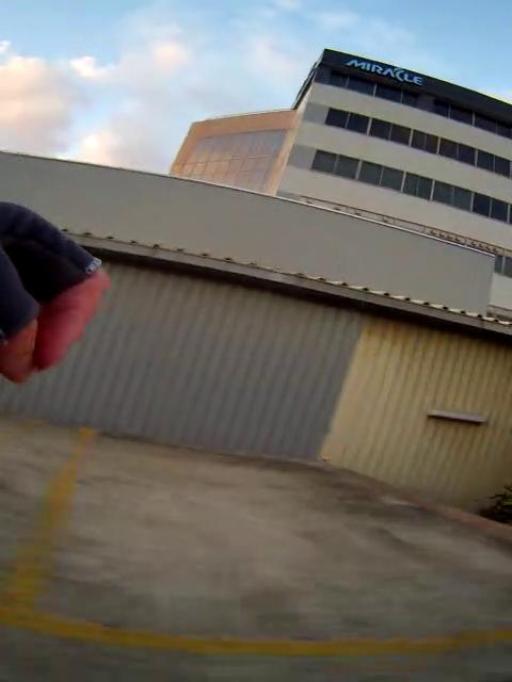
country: JP
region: Osaka
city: Suita
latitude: 34.7342
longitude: 135.5227
